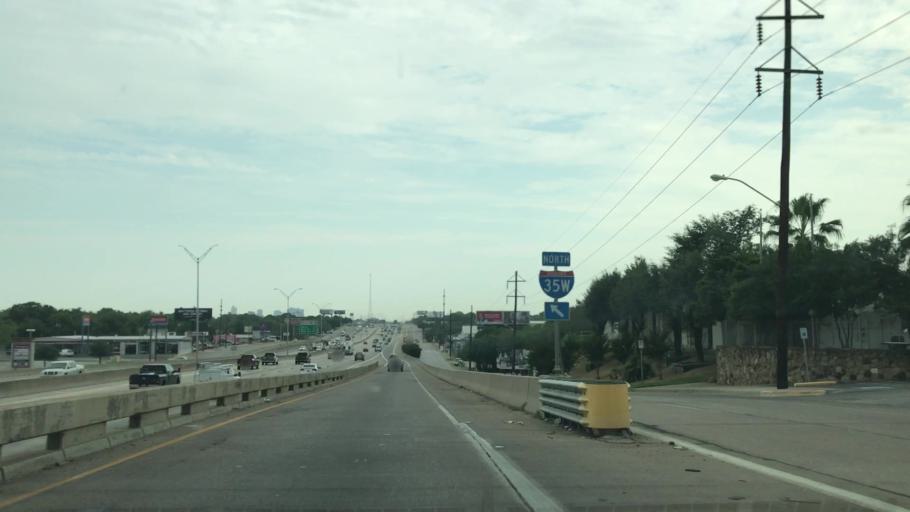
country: US
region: Texas
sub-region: Tarrant County
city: Edgecliff Village
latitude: 32.6863
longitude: -97.3204
